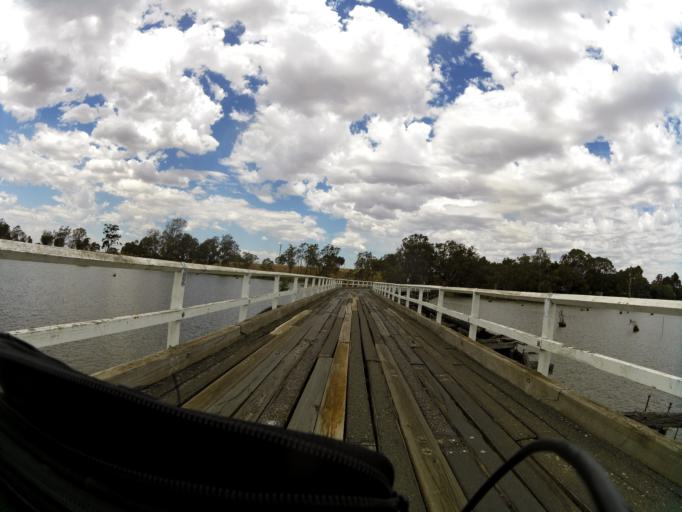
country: AU
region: Victoria
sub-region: Campaspe
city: Kyabram
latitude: -36.7455
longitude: 145.1394
